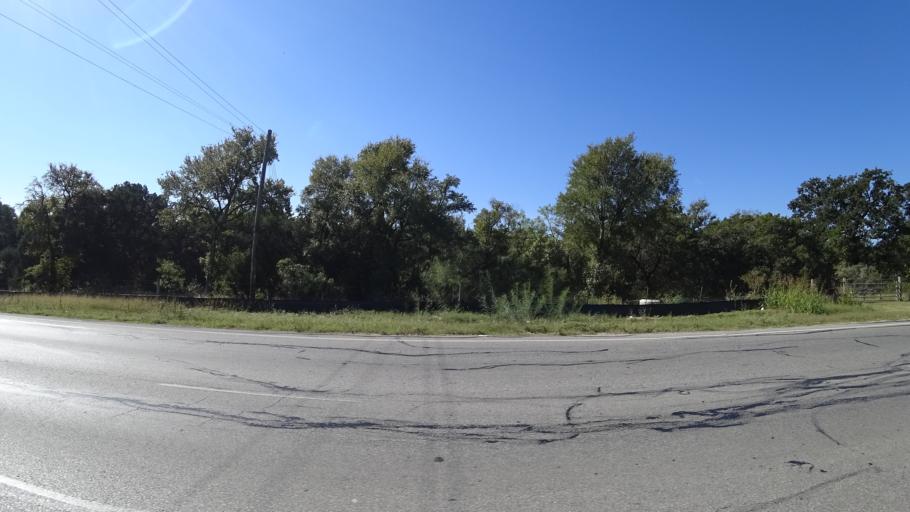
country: US
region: Texas
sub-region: Travis County
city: Hornsby Bend
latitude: 30.2607
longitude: -97.6189
